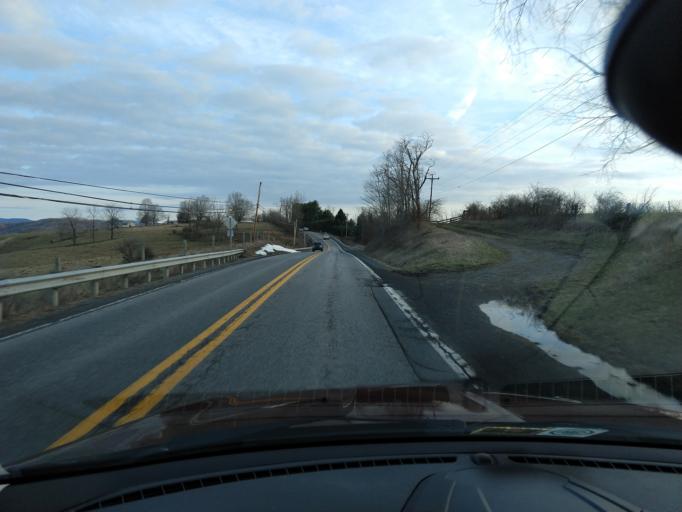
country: US
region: West Virginia
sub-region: Greenbrier County
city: Lewisburg
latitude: 37.9091
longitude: -80.3846
